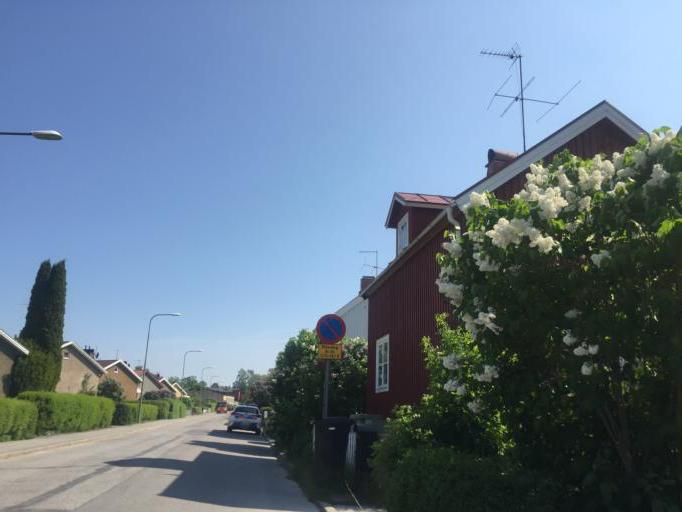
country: SE
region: Stockholm
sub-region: Stockholms Kommun
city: Arsta
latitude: 59.2746
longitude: 18.0731
